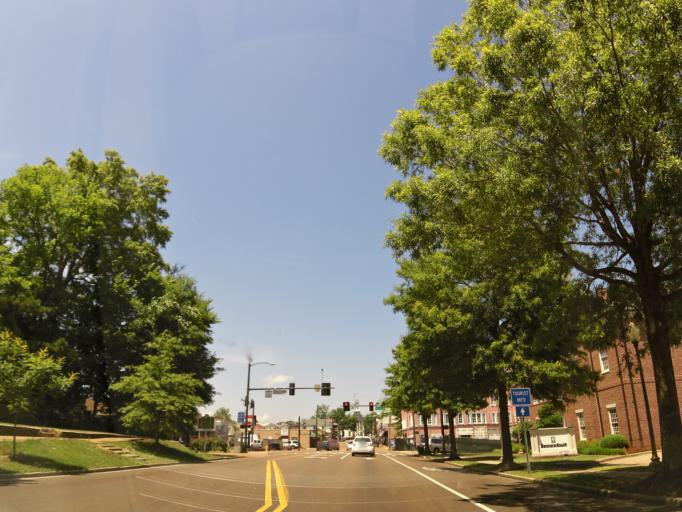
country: US
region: Mississippi
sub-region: Lafayette County
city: Oxford
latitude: 34.3635
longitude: -89.5193
